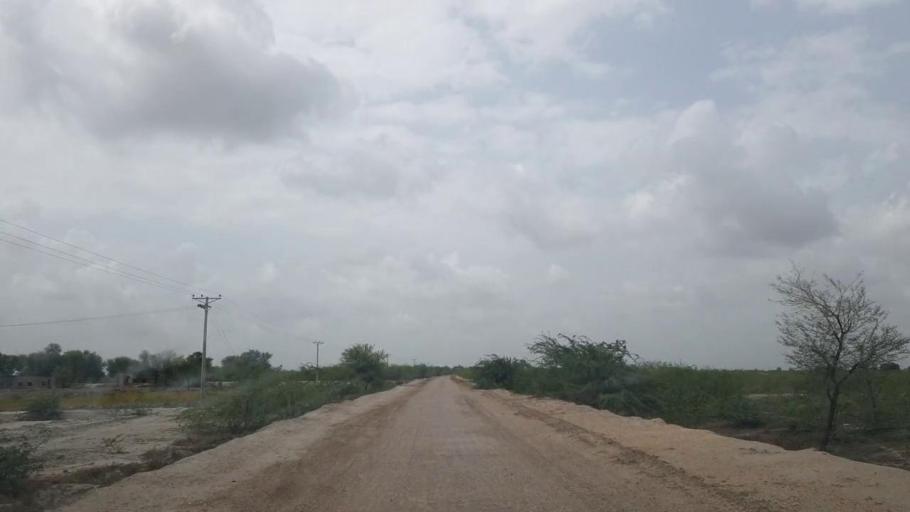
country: PK
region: Sindh
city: Naukot
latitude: 24.9492
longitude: 69.2583
